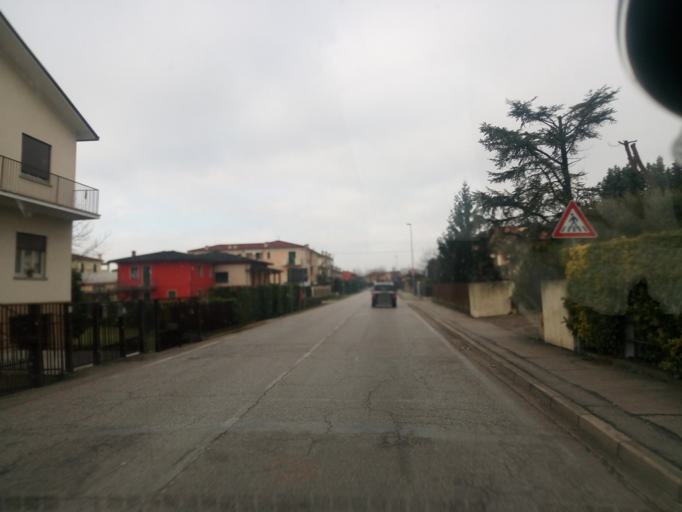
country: IT
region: Veneto
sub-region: Provincia di Vicenza
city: Sandrigo
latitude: 45.6636
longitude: 11.5945
